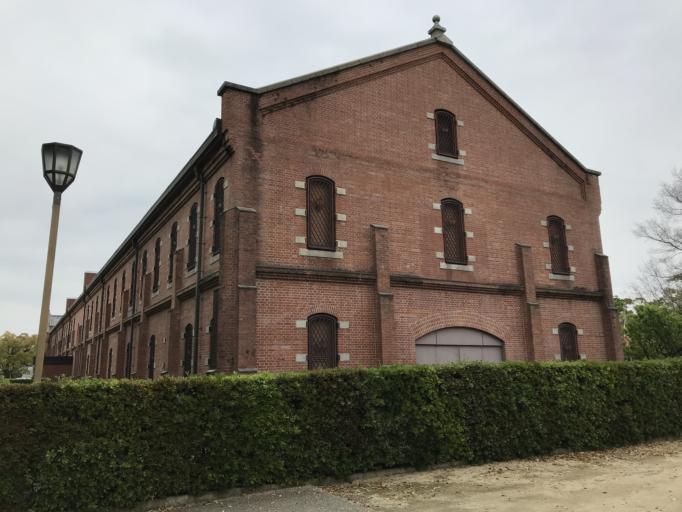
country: JP
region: Hyogo
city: Himeji
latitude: 34.8389
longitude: 134.6962
